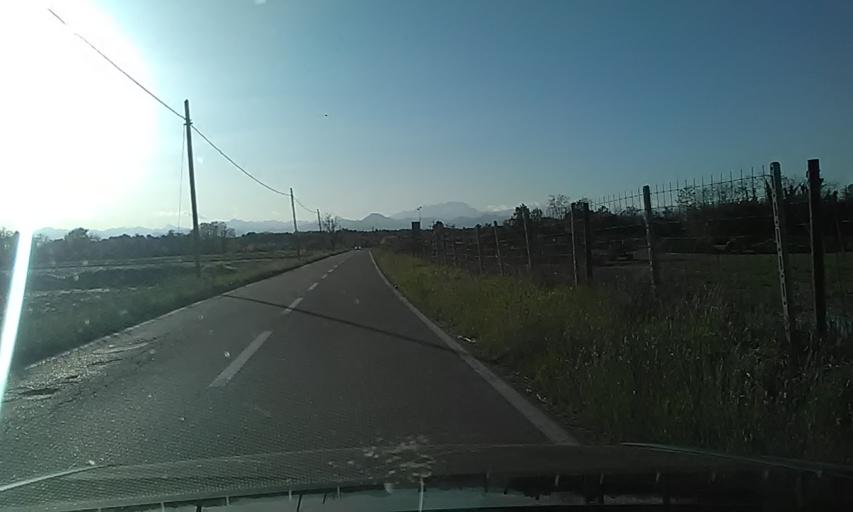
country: IT
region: Piedmont
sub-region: Provincia di Novara
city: Barengo
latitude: 45.5700
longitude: 8.5308
